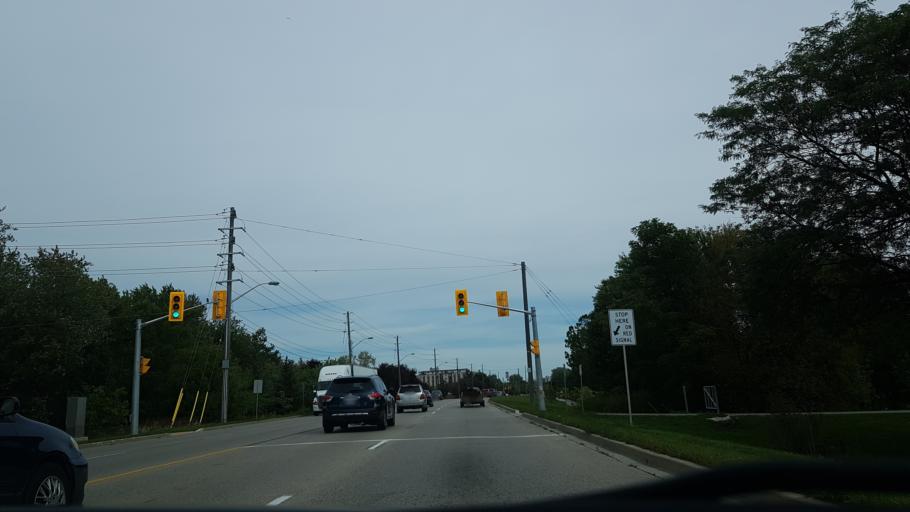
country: CA
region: Ontario
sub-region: Wellington County
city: Guelph
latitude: 43.5310
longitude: -80.2582
